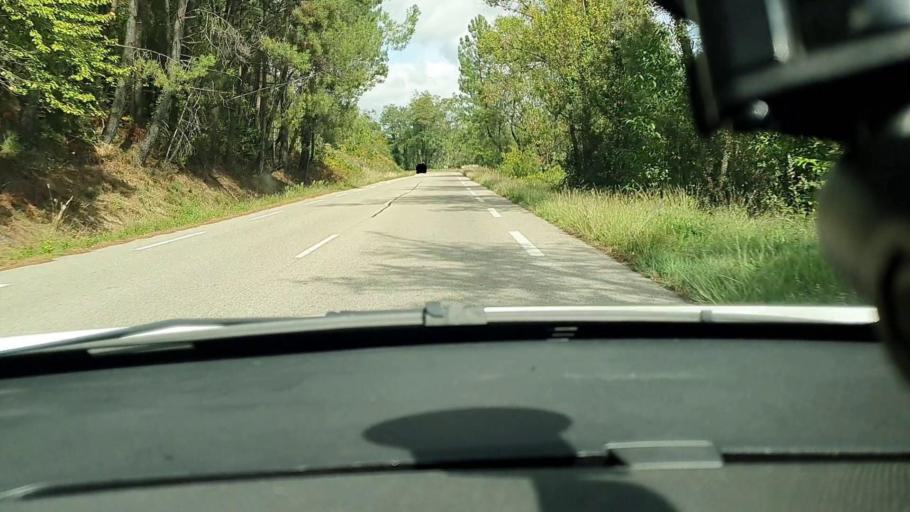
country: FR
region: Languedoc-Roussillon
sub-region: Departement du Gard
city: Les Salles-du-Gardon
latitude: 44.2263
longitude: 4.0518
